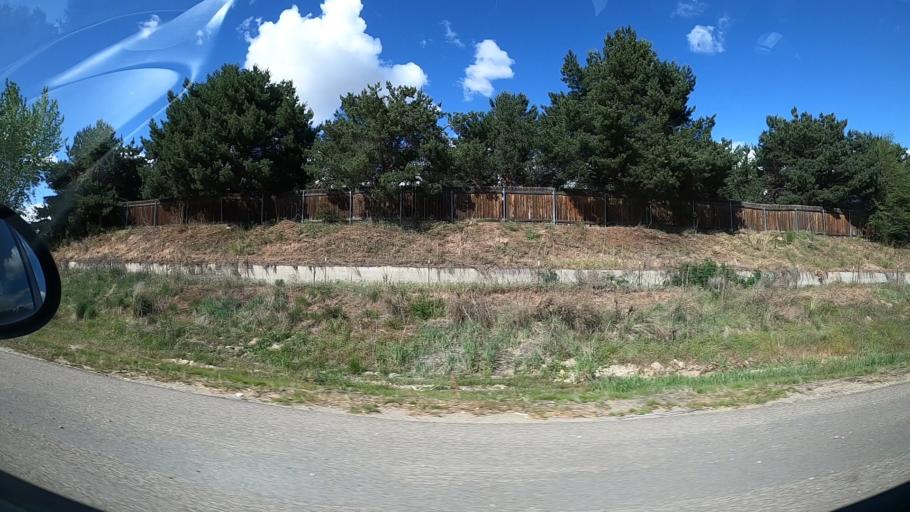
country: US
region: Idaho
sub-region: Ada County
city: Eagle
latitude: 43.6927
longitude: -116.3731
